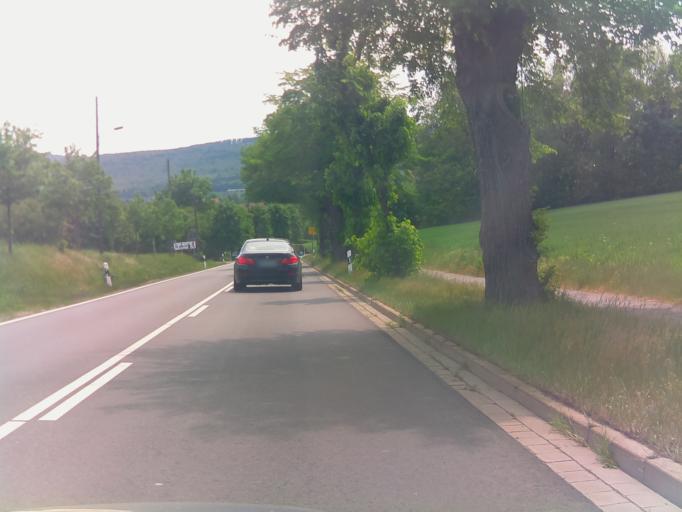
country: DE
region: Saxony-Anhalt
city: Blankenburg
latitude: 51.7813
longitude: 10.9684
